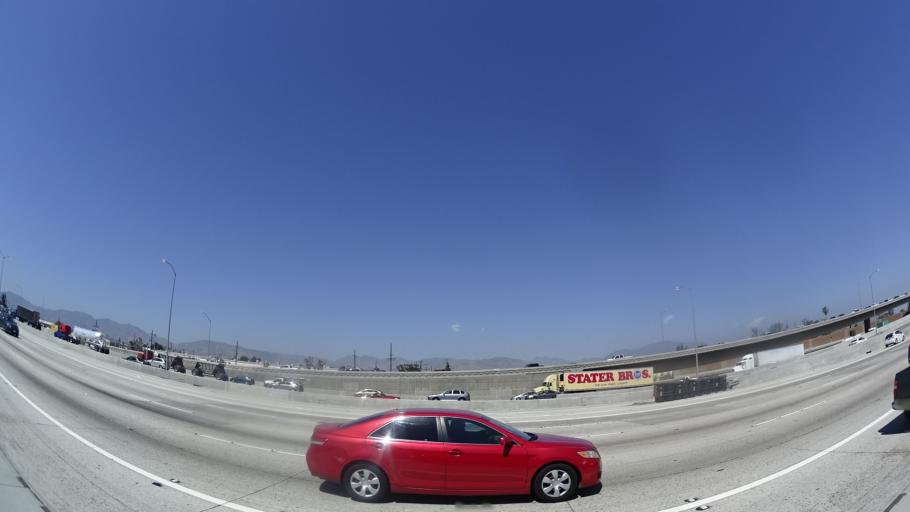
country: US
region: California
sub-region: Los Angeles County
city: San Fernando
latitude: 34.2355
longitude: -118.4131
